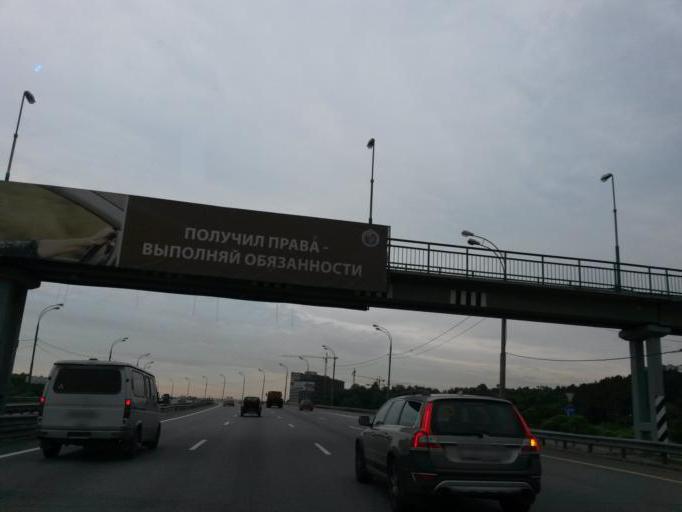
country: RU
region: Moskovskaya
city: Vidnoye
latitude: 55.5450
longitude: 37.6942
